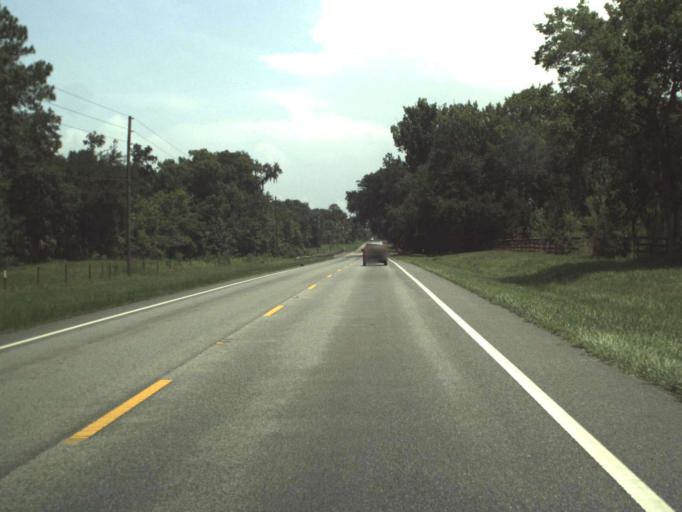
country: US
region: Florida
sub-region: Sumter County
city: Lake Panasoffkee
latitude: 28.7681
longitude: -82.0641
